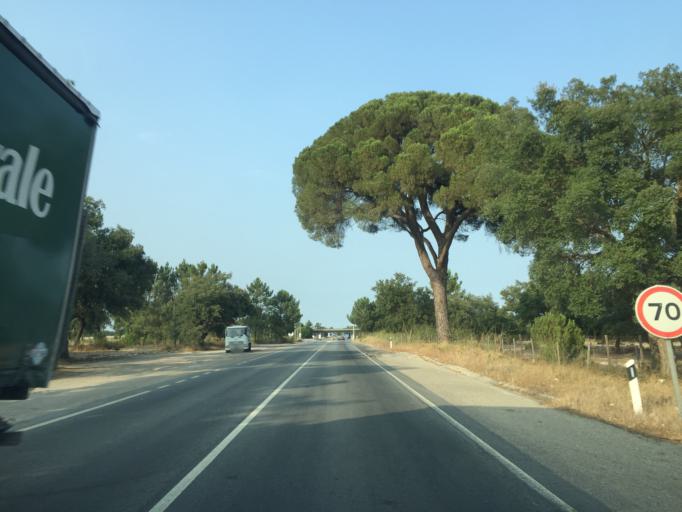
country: PT
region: Setubal
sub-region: Setubal
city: Setubal
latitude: 38.5917
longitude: -8.6750
